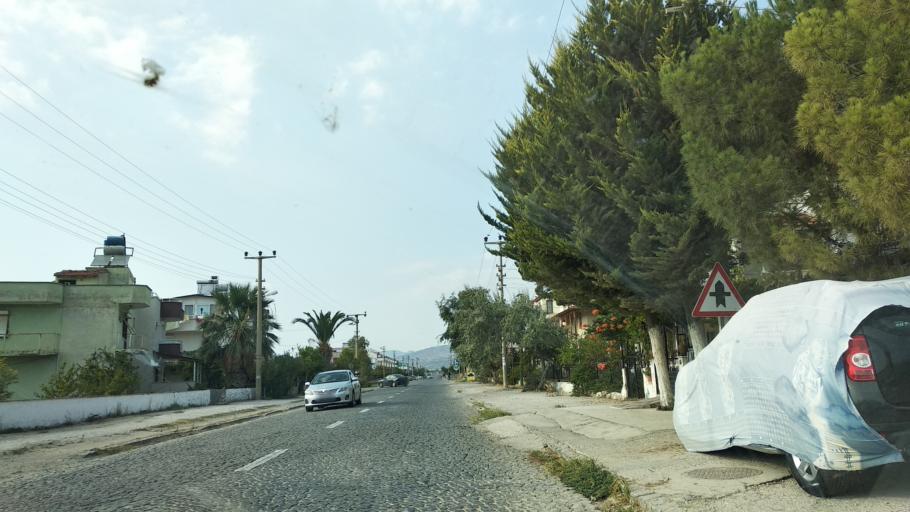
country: TR
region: Izmir
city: Dikili
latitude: 39.0991
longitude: 26.8828
